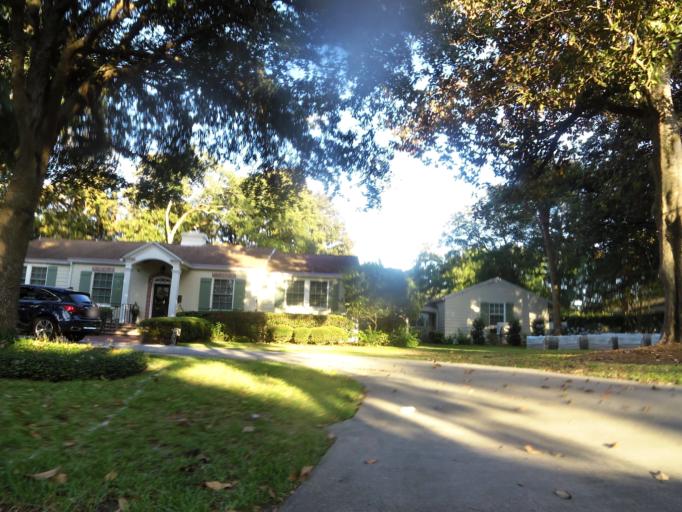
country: US
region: Florida
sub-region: Clay County
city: Orange Park
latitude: 30.2471
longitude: -81.6884
